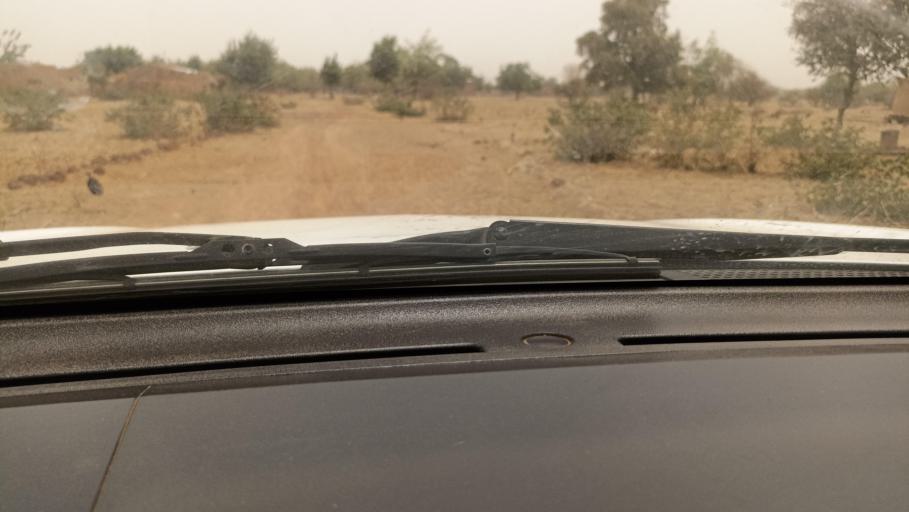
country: BF
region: Boucle du Mouhoun
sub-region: Province du Nayala
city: Toma
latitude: 12.8665
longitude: -2.7482
